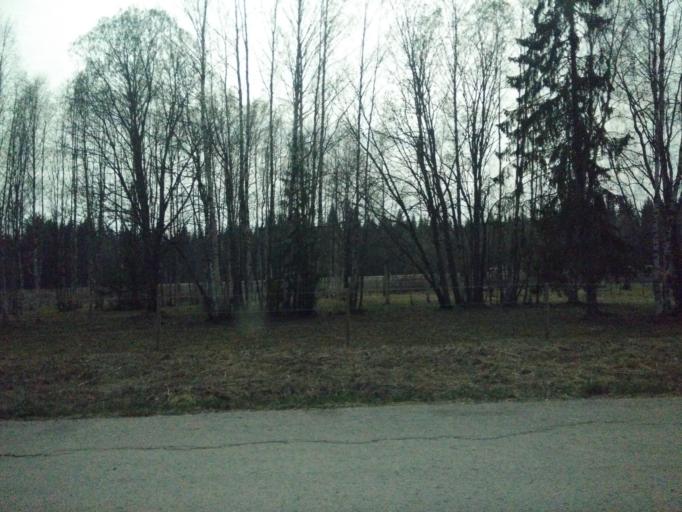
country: SE
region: Vaermland
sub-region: Munkfors Kommun
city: Munkfors
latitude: 59.8373
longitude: 13.5068
